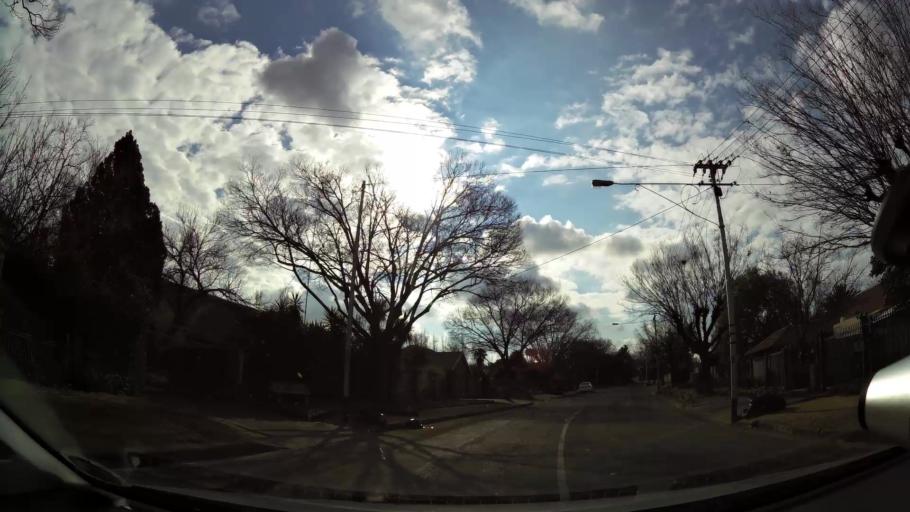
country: ZA
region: Orange Free State
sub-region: Mangaung Metropolitan Municipality
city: Bloemfontein
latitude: -29.0843
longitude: 26.2107
